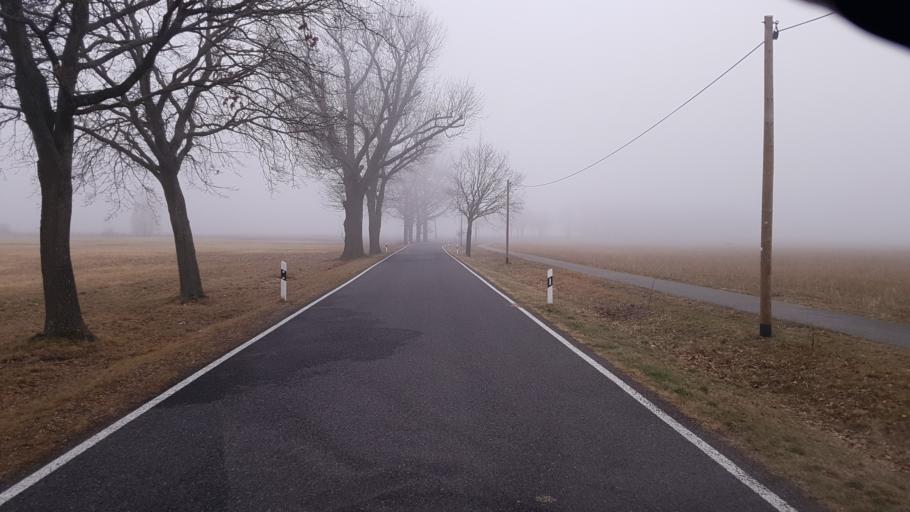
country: DE
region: Saxony-Anhalt
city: Holzdorf
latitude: 51.8583
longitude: 13.2110
